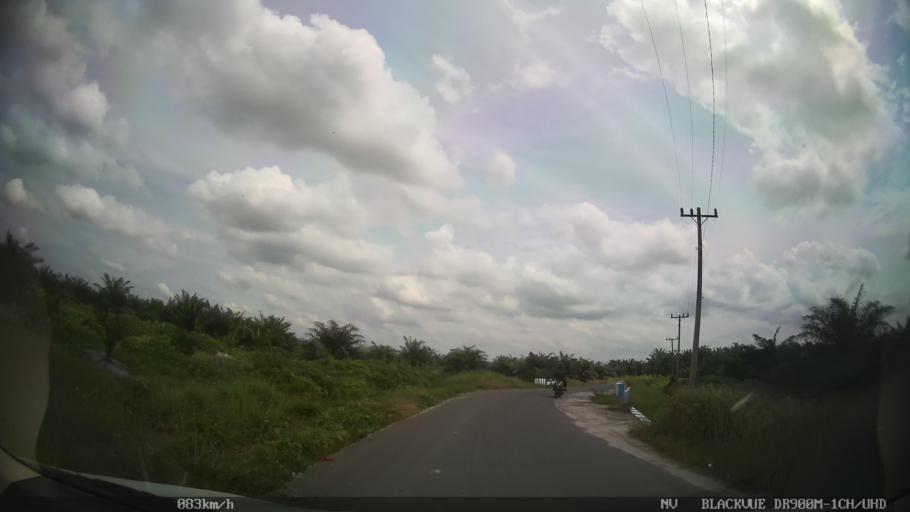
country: ID
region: North Sumatra
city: Percut
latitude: 3.5893
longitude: 98.8410
